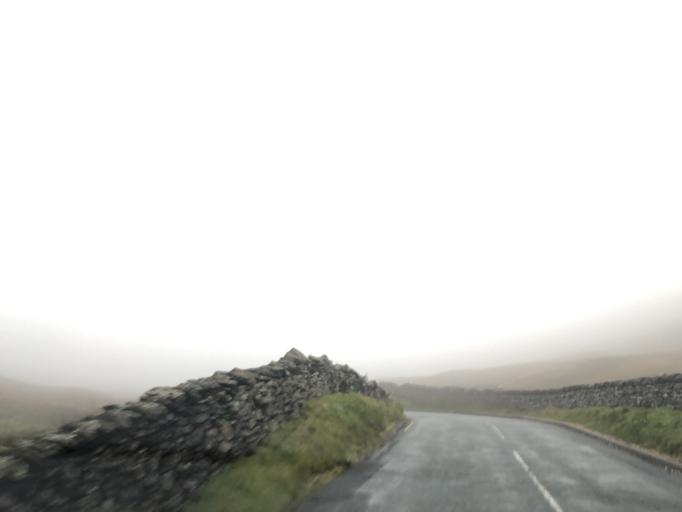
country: GB
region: England
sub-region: Cumbria
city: Ambleside
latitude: 54.4689
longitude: -2.9235
